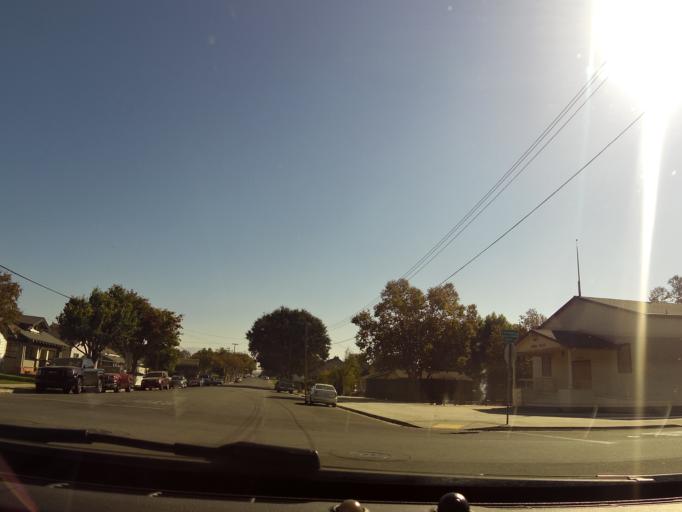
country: US
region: California
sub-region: San Benito County
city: Hollister
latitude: 36.8495
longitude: -121.4095
